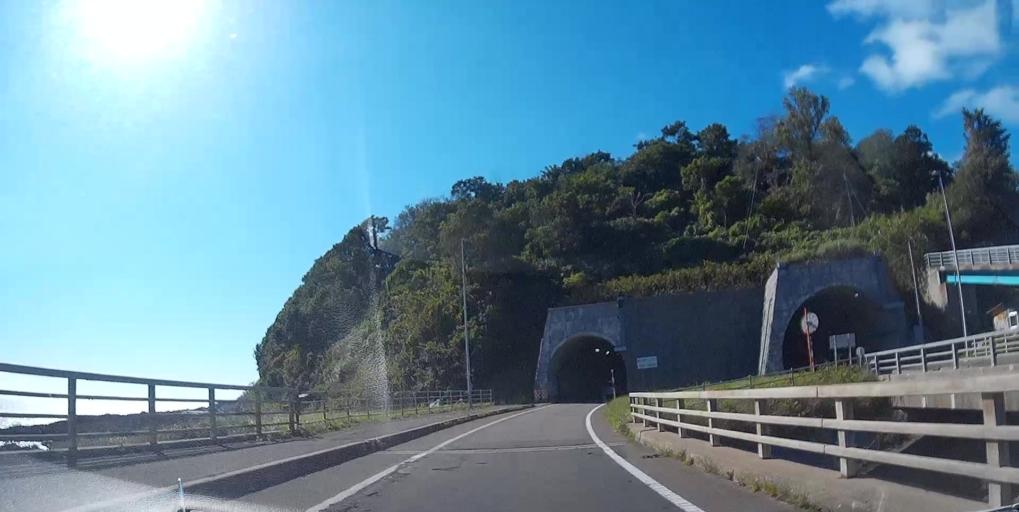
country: JP
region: Hokkaido
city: Kamiiso
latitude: 42.0369
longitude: 140.0895
